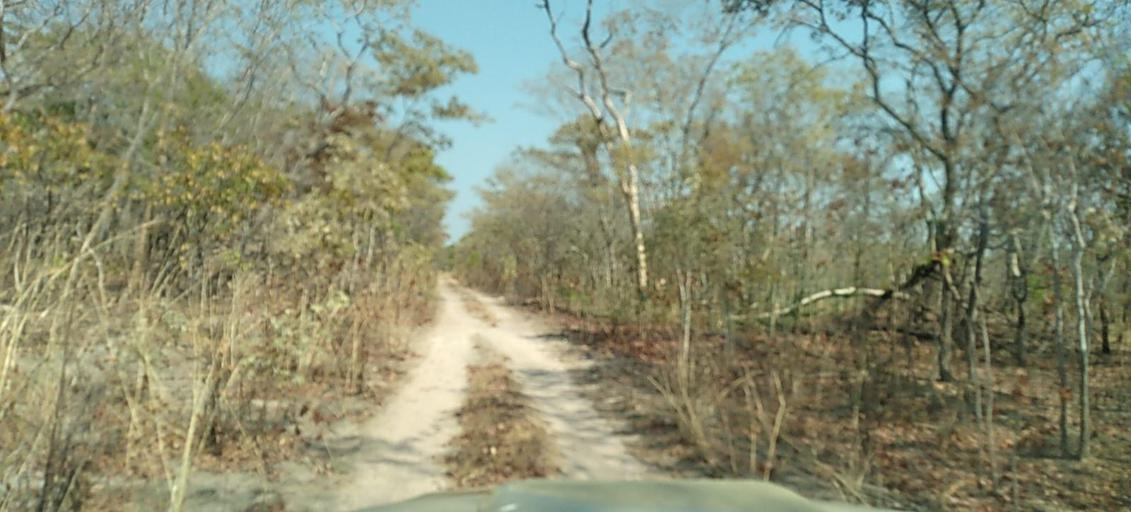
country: ZM
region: North-Western
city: Kalengwa
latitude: -13.3274
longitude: 24.8322
